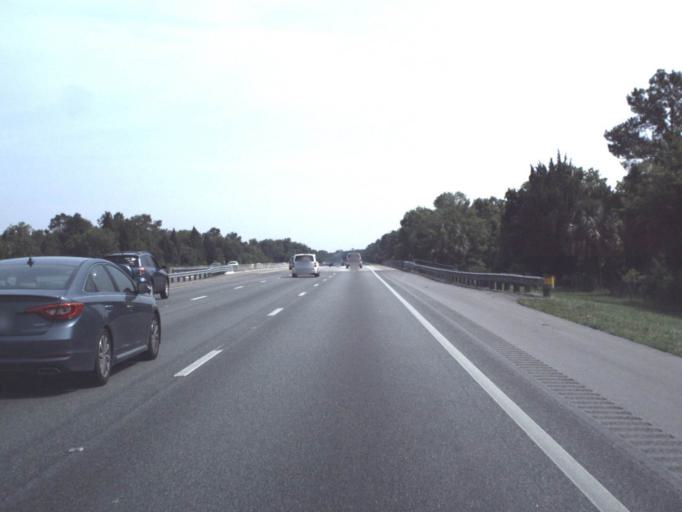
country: US
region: Florida
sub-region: Nassau County
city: Yulee
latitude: 30.5869
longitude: -81.6464
